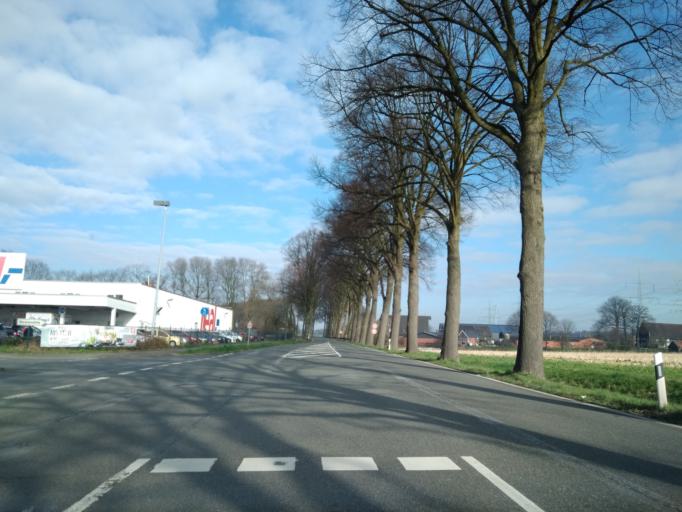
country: DE
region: North Rhine-Westphalia
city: Marl
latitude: 51.6187
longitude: 7.0798
